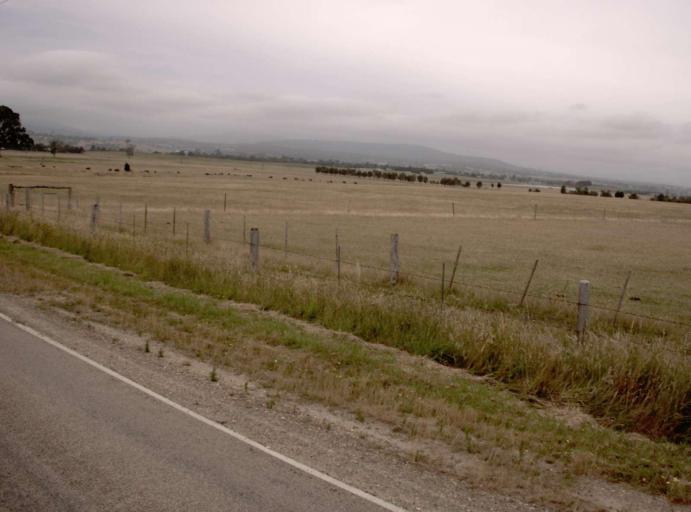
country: AU
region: Victoria
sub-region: East Gippsland
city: Bairnsdale
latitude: -37.8152
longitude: 147.4366
